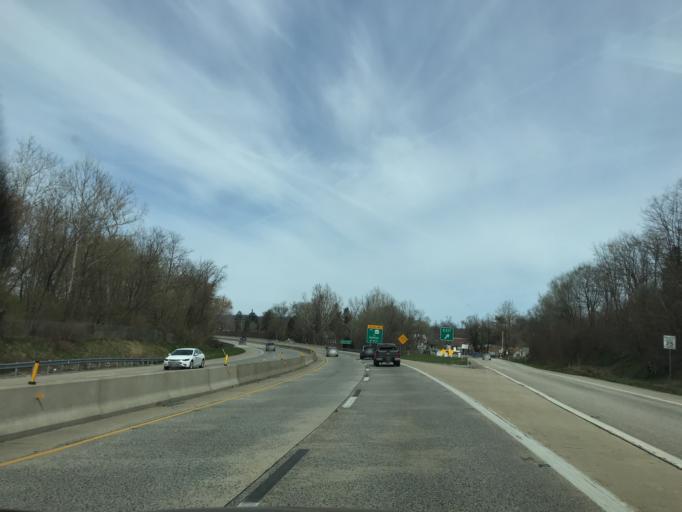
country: US
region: Pennsylvania
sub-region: Perry County
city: Marysville
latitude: 40.3632
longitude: -76.9271
